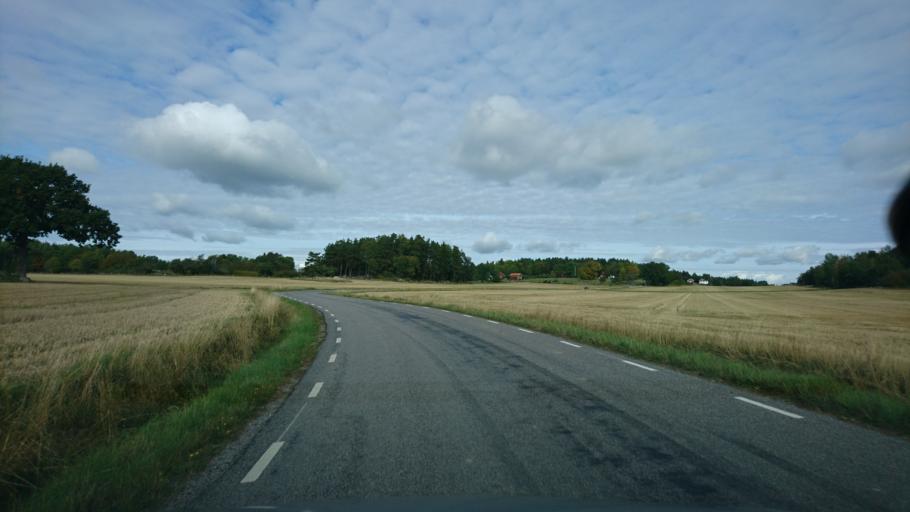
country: SE
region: Soedermanland
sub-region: Strangnas Kommun
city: Stallarholmen
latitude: 59.3830
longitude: 17.2618
